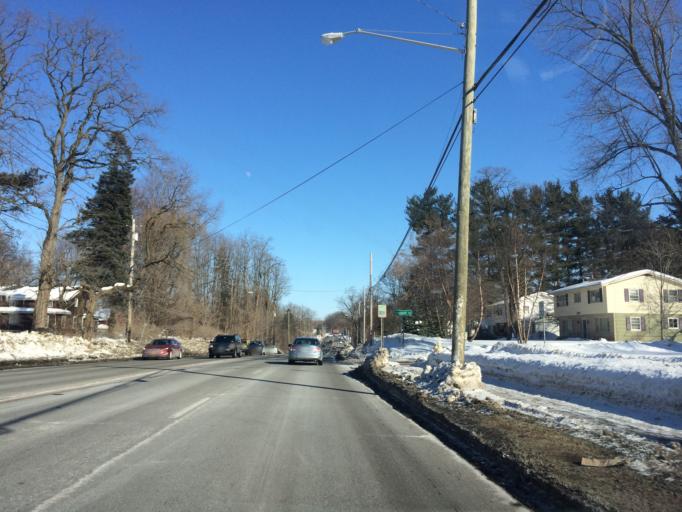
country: US
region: New York
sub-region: Monroe County
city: East Rochester
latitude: 43.1022
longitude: -77.4739
